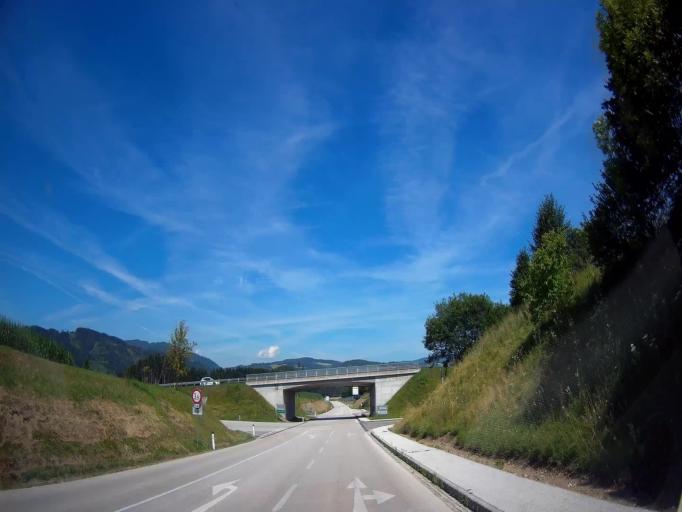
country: AT
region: Carinthia
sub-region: Politischer Bezirk Sankt Veit an der Glan
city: St. Georgen am Laengsee
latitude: 46.8036
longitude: 14.4103
